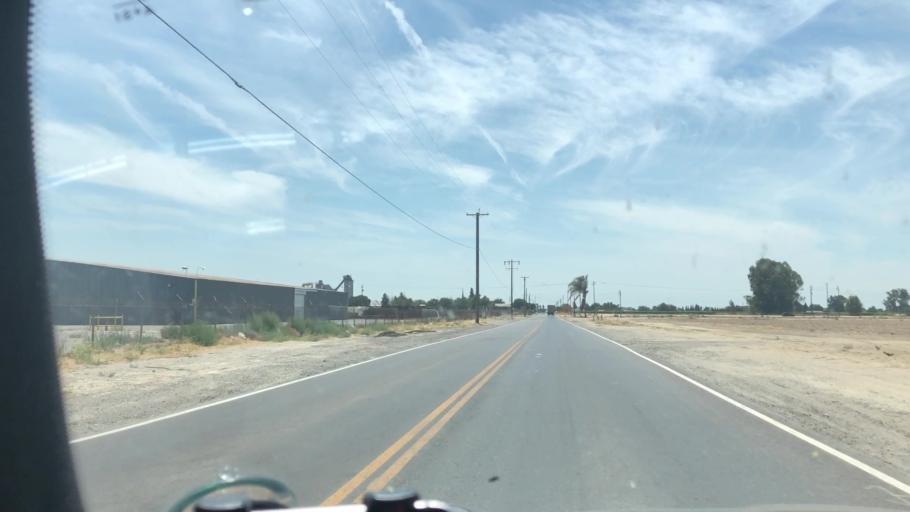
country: US
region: California
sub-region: Fresno County
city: Easton
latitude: 36.6814
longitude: -119.7547
